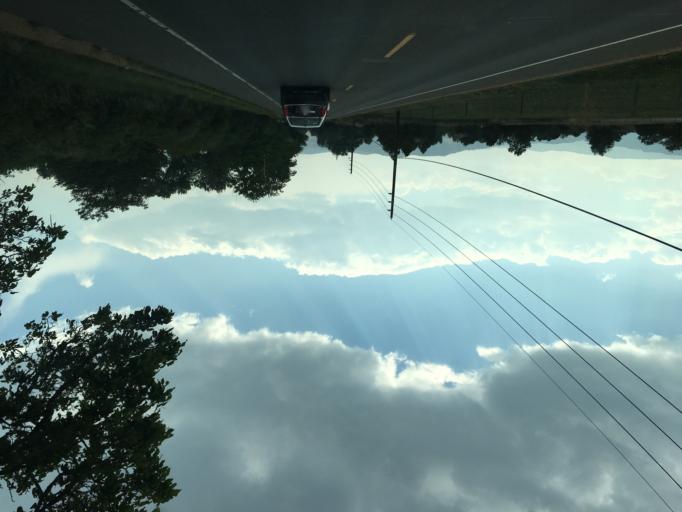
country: US
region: Colorado
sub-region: Boulder County
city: Gunbarrel
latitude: 40.0510
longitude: -105.2099
